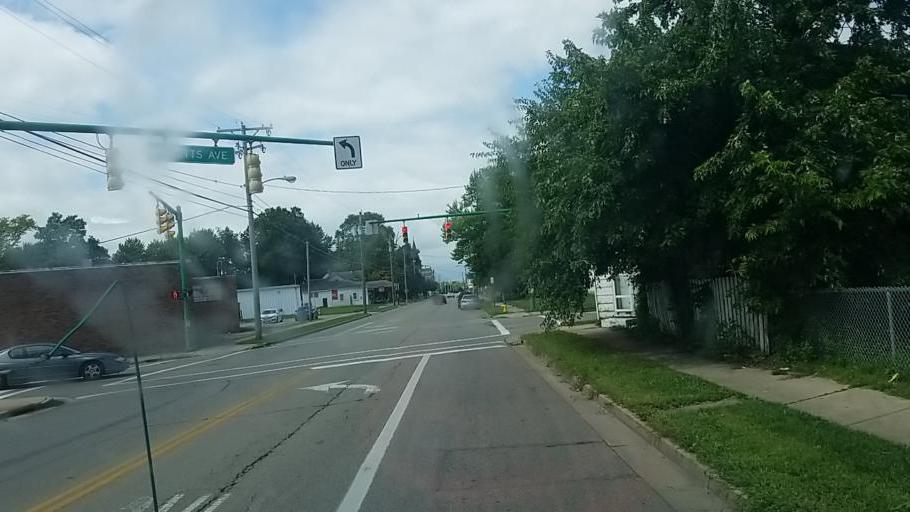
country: US
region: Ohio
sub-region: Clark County
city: Springfield
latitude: 39.9144
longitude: -83.8008
